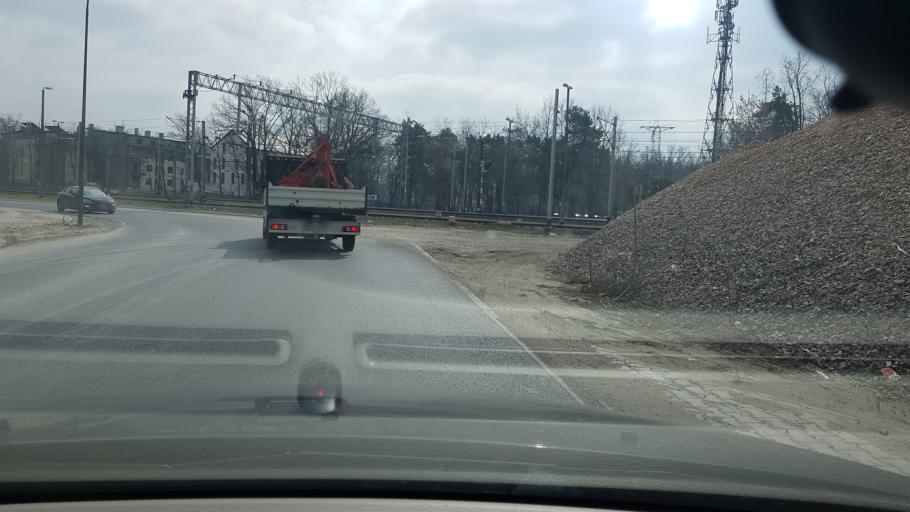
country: PL
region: Masovian Voivodeship
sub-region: Warszawa
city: Rembertow
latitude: 52.2580
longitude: 21.1528
